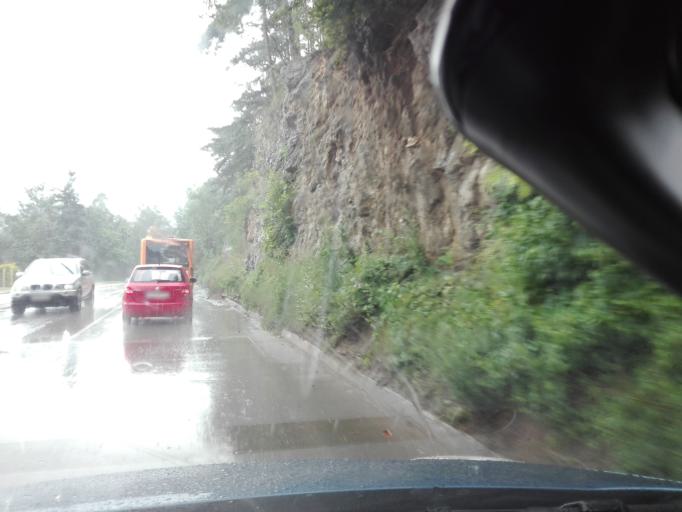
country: BG
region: Sofia-Capital
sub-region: Stolichna Obshtina
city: Sofia
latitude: 42.6023
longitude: 23.4028
